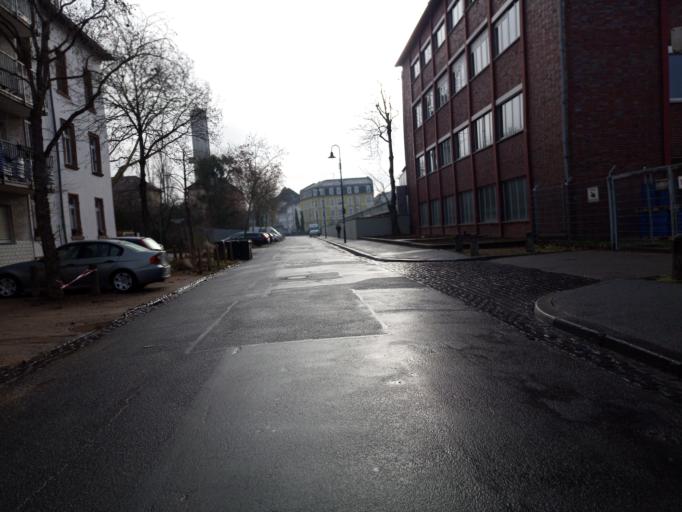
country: DE
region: Hesse
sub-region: Regierungsbezirk Darmstadt
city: Darmstadt
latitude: 49.8762
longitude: 8.6387
